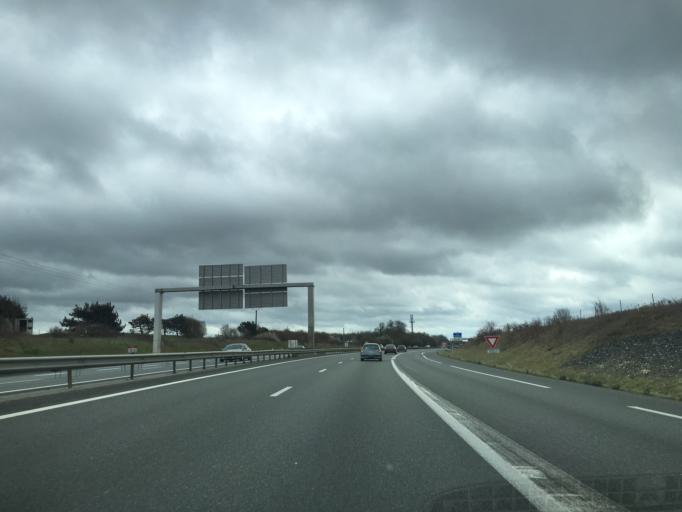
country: FR
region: Ile-de-France
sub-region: Departement de Seine-et-Marne
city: Brie-Comte-Robert
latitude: 48.6526
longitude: 2.6177
